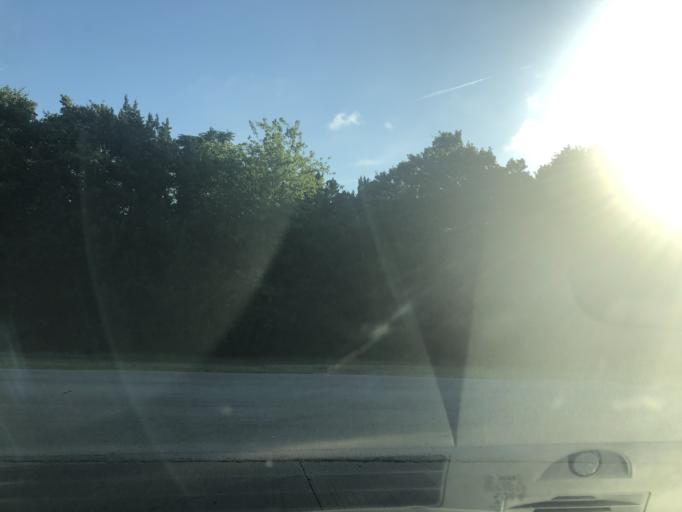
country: US
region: Texas
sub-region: Dallas County
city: Duncanville
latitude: 32.6649
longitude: -96.9511
